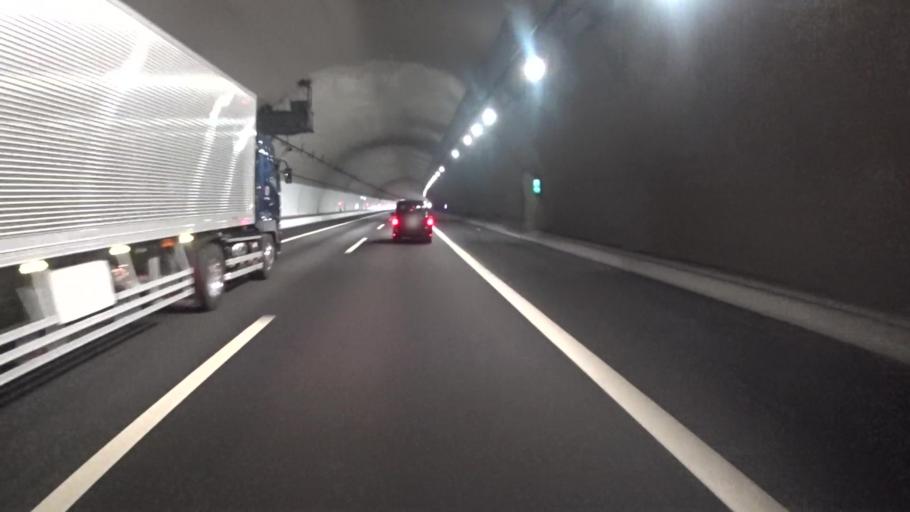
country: JP
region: Shiga Prefecture
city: Minakuchicho-matoba
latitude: 34.9219
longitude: 136.1265
